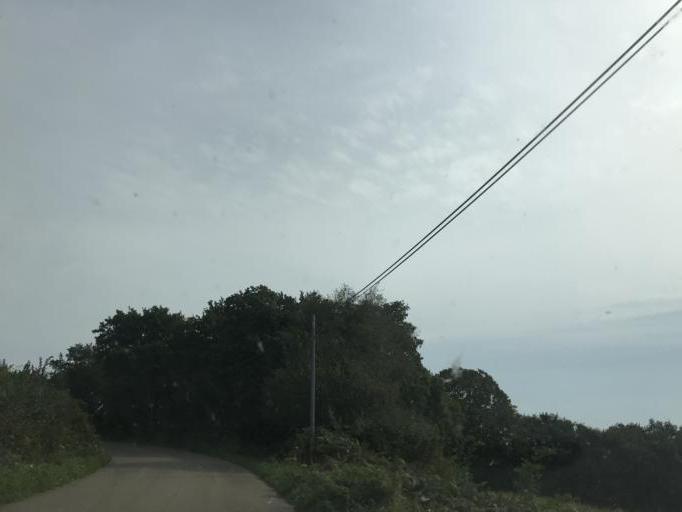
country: FR
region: Brittany
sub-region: Departement du Finistere
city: Brasparts
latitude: 48.3252
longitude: -3.9224
